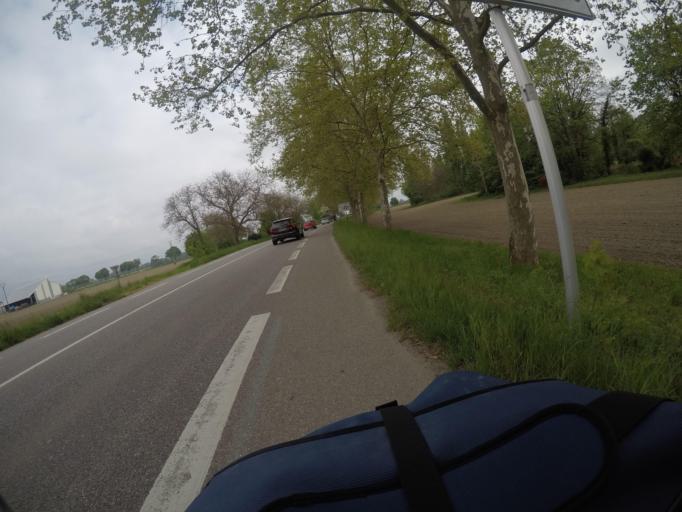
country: FR
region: Alsace
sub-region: Departement du Bas-Rhin
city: La Wantzenau
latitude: 48.6667
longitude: 7.8252
